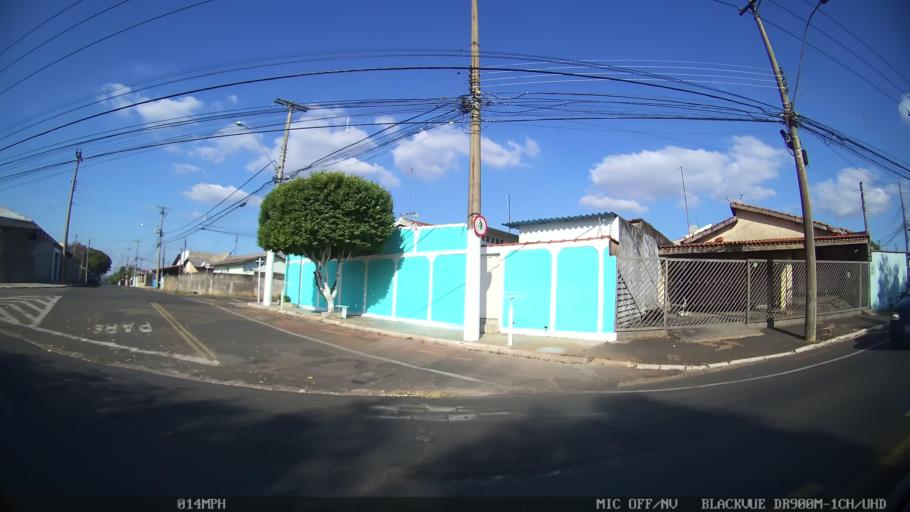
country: BR
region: Sao Paulo
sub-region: Nova Odessa
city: Nova Odessa
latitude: -22.7878
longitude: -47.3027
